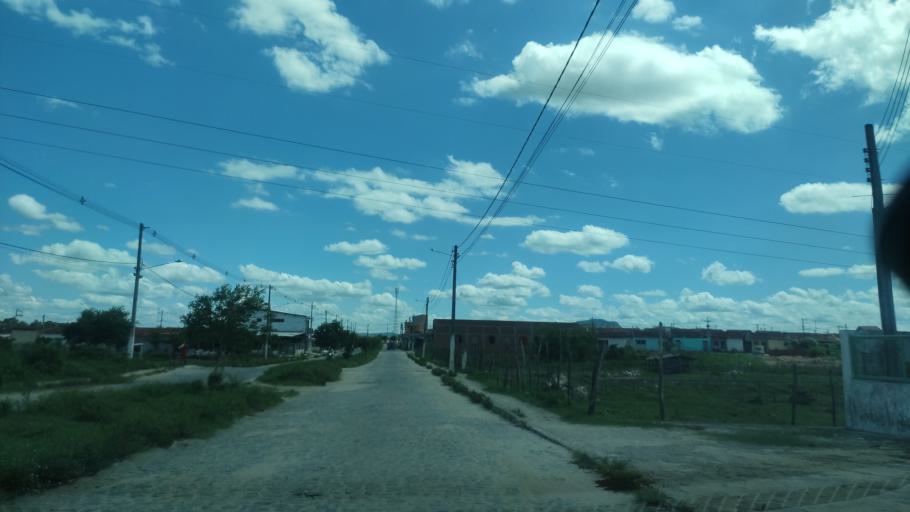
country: BR
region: Alagoas
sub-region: Uniao Dos Palmares
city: Uniao dos Palmares
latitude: -9.1494
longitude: -36.0071
